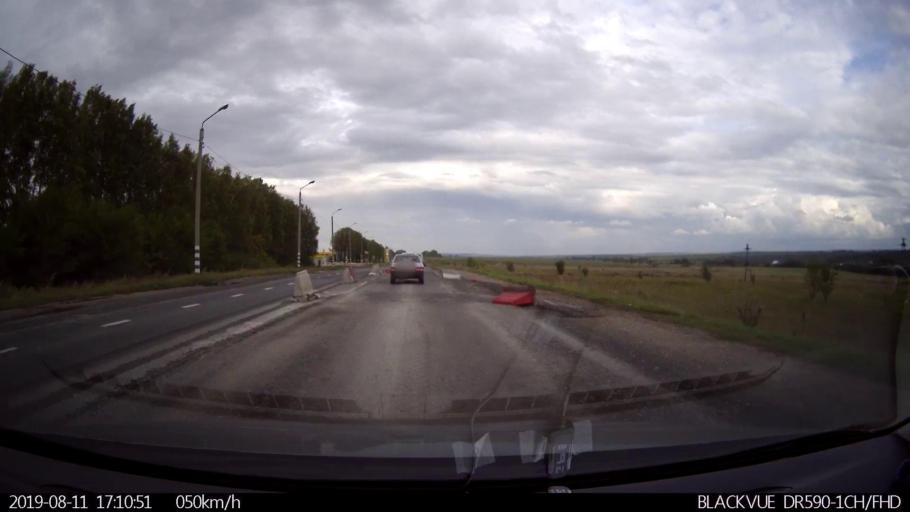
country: RU
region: Ulyanovsk
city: Mayna
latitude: 54.2991
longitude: 47.8787
